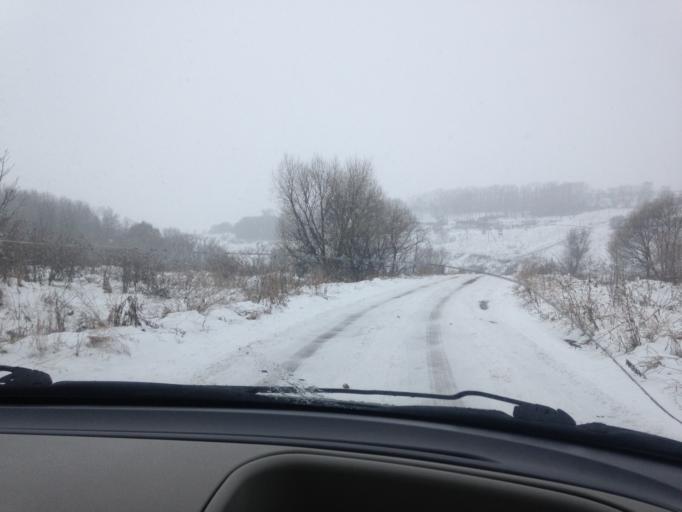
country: RU
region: Tula
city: Shchekino
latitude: 53.8203
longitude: 37.5047
